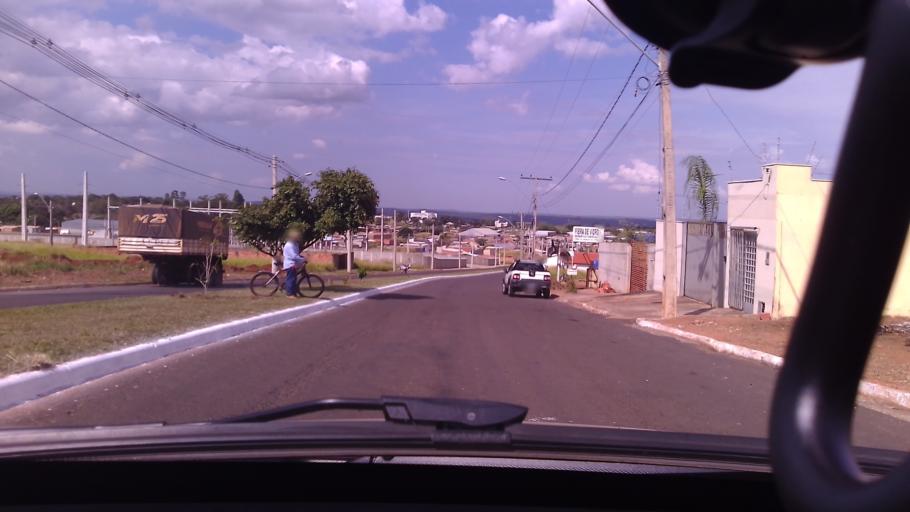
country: BR
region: Goias
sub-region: Mineiros
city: Mineiros
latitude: -17.5480
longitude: -52.5319
